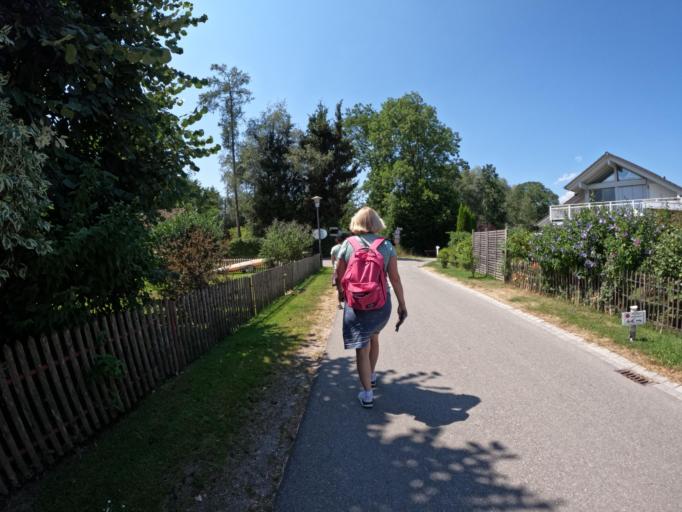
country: DE
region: Bavaria
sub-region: Upper Bavaria
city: Ubersee
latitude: 47.8373
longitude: 12.4814
